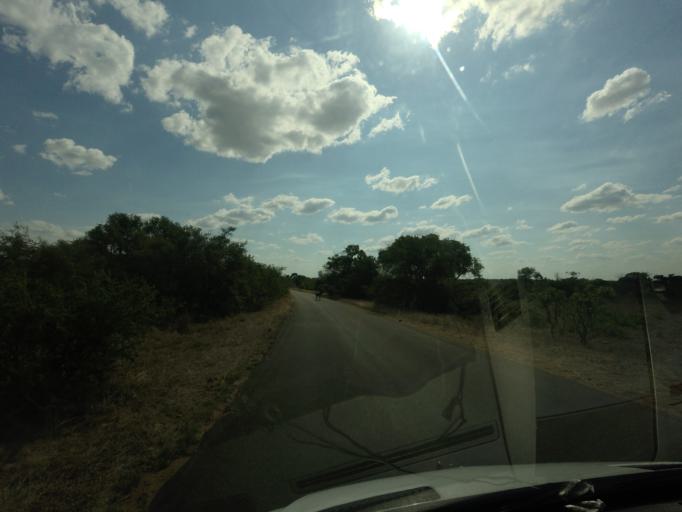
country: ZA
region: Limpopo
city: Thulamahashi
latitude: -24.3961
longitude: 31.5915
